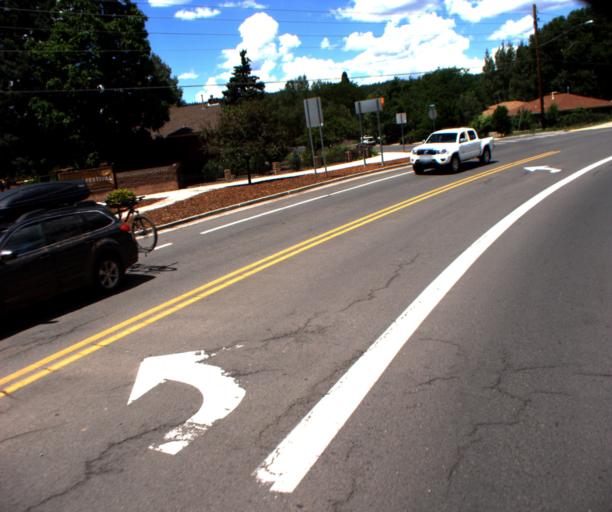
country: US
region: Arizona
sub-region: Coconino County
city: Flagstaff
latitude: 35.2069
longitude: -111.6482
